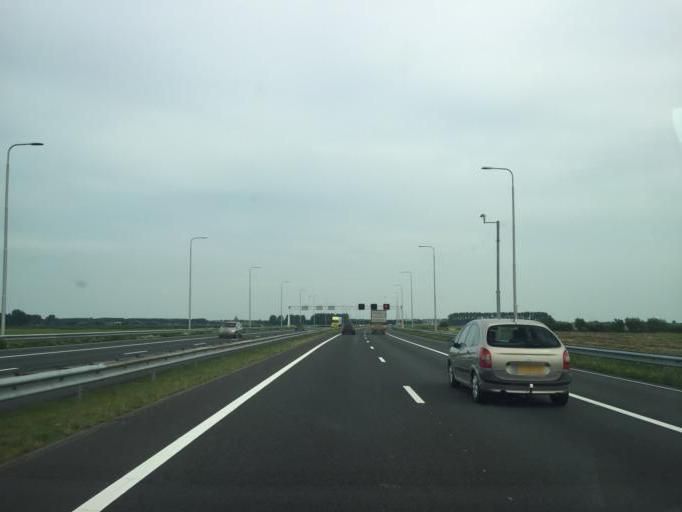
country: NL
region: North Holland
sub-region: Gemeente Heiloo
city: Heiloo
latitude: 52.5712
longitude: 4.7161
